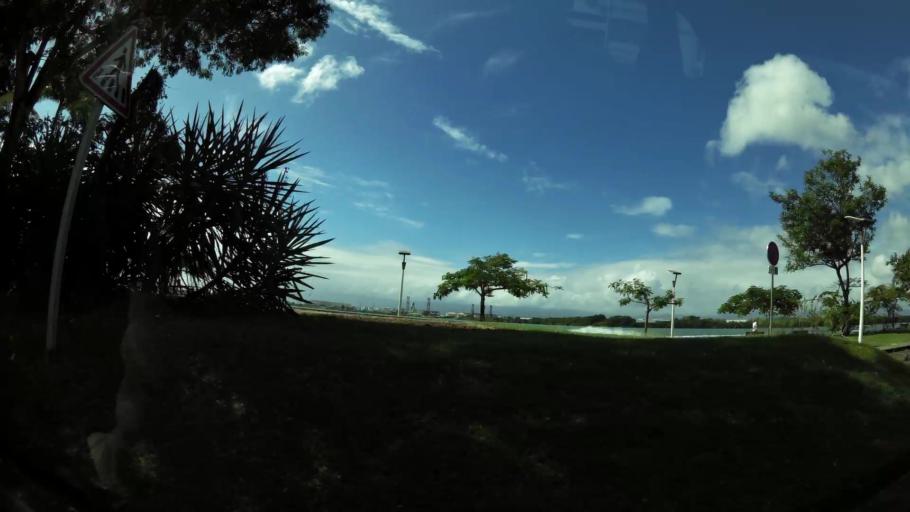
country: GP
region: Guadeloupe
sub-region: Guadeloupe
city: Pointe-a-Pitre
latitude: 16.2454
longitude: -61.5427
